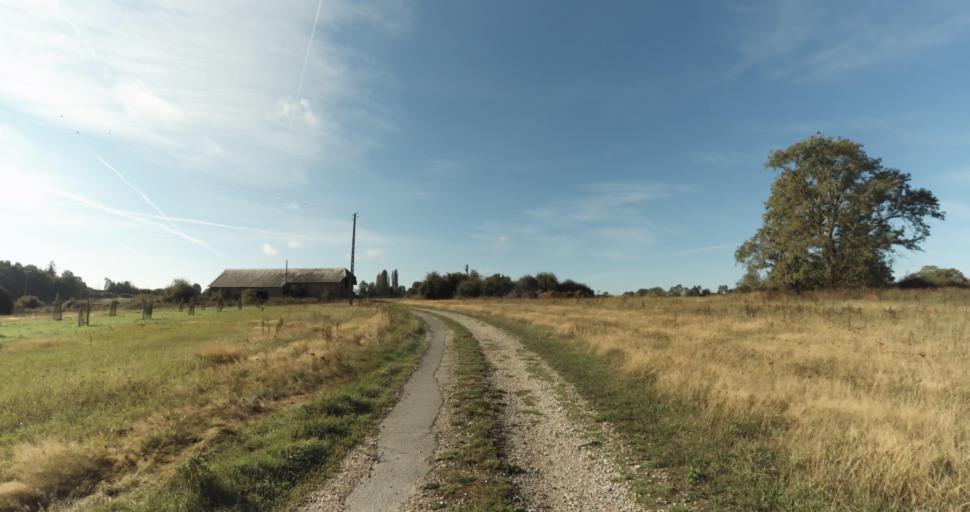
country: FR
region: Lower Normandy
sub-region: Departement de l'Orne
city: Vimoutiers
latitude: 48.9316
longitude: 0.2918
